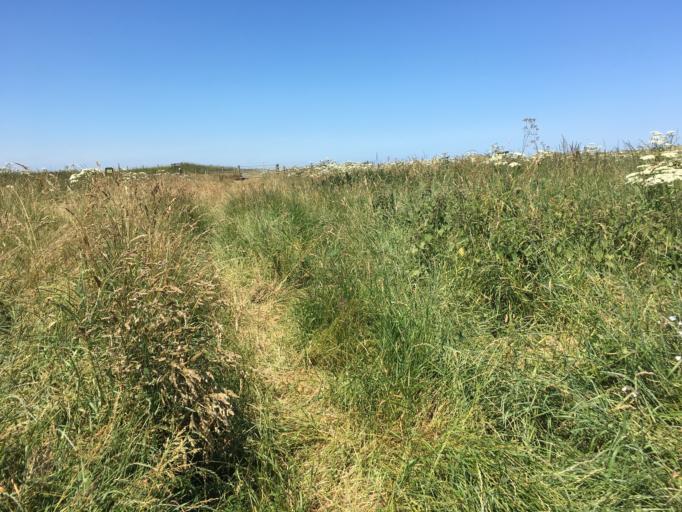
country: GB
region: England
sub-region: Northumberland
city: Ancroft
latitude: 55.7159
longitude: -1.9374
